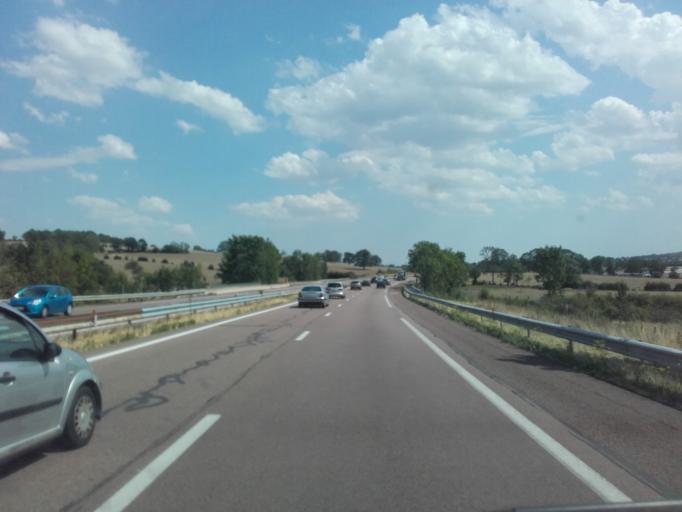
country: FR
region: Bourgogne
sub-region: Departement de l'Yonne
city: Avallon
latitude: 47.5498
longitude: 3.9630
